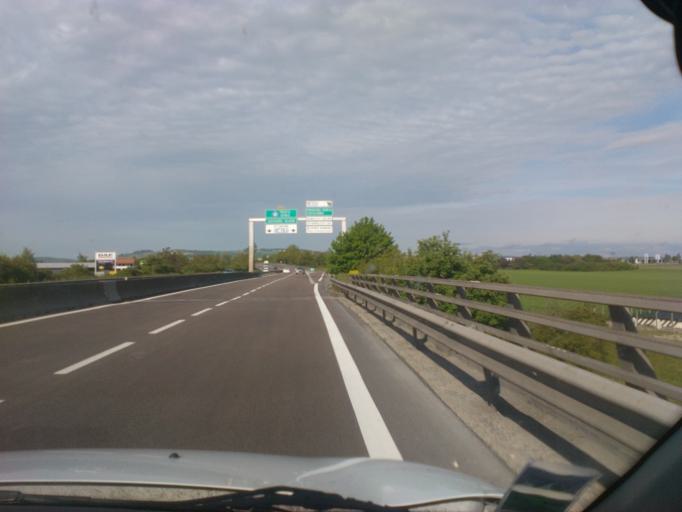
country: FR
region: Champagne-Ardenne
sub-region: Departement de l'Aube
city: La Chapelle-Saint-Luc
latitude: 48.3282
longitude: 4.0356
